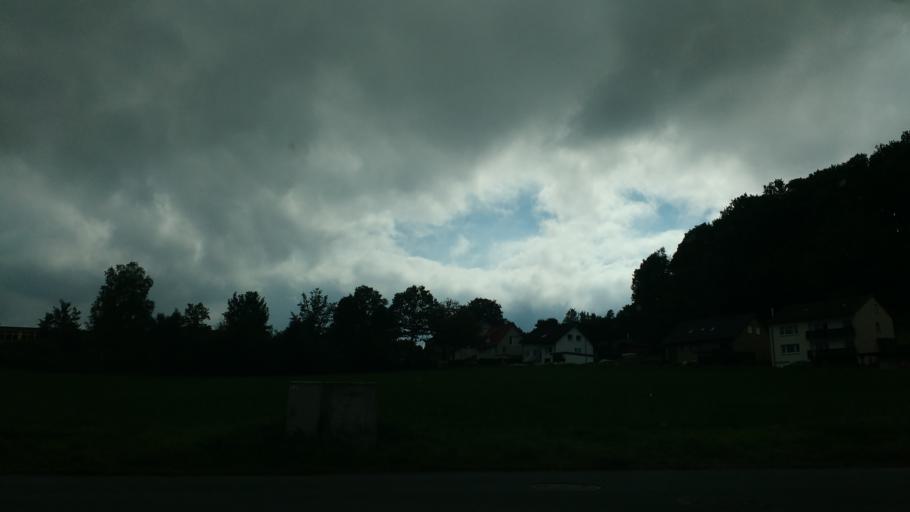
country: DE
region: North Rhine-Westphalia
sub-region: Regierungsbezirk Detmold
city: Altenbeken
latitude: 51.7609
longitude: 8.9405
